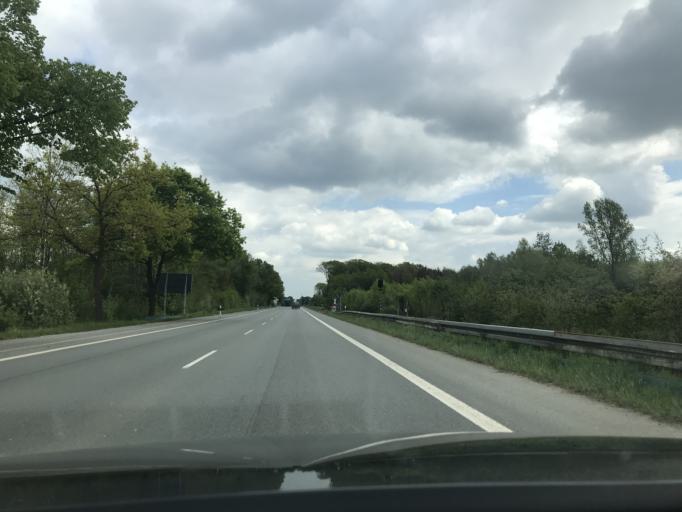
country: DE
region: North Rhine-Westphalia
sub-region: Regierungsbezirk Detmold
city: Rheda-Wiedenbruck
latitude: 51.8683
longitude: 8.2618
